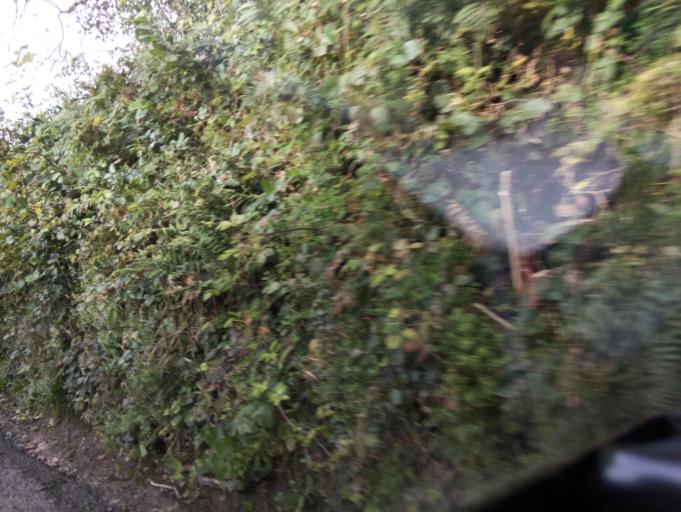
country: GB
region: England
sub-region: Devon
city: South Brent
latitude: 50.3994
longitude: -3.7808
